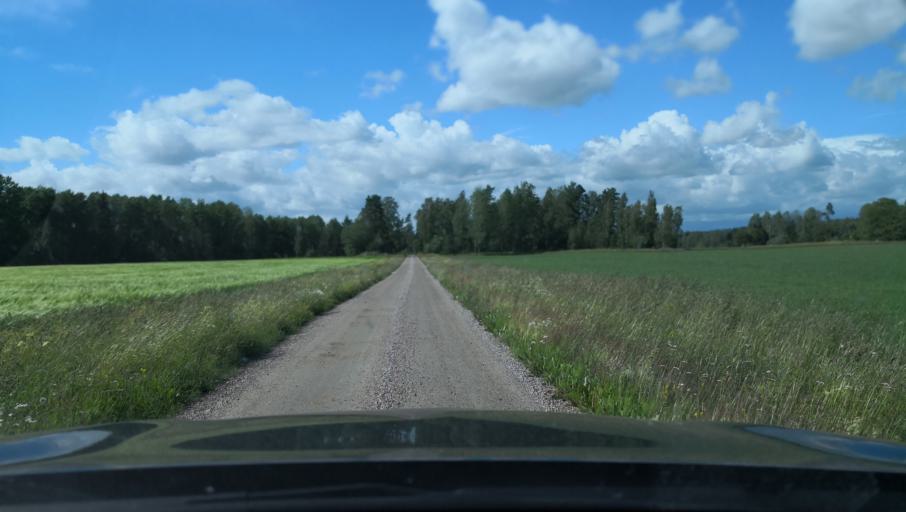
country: SE
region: Vaestmanland
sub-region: Kungsors Kommun
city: Kungsoer
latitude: 59.3219
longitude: 16.0498
